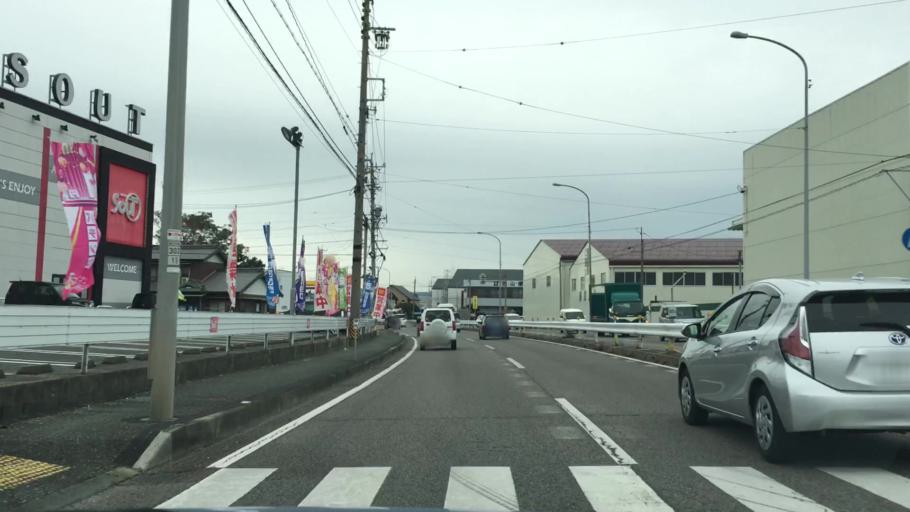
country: JP
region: Aichi
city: Kozakai-cho
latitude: 34.8098
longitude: 137.3568
